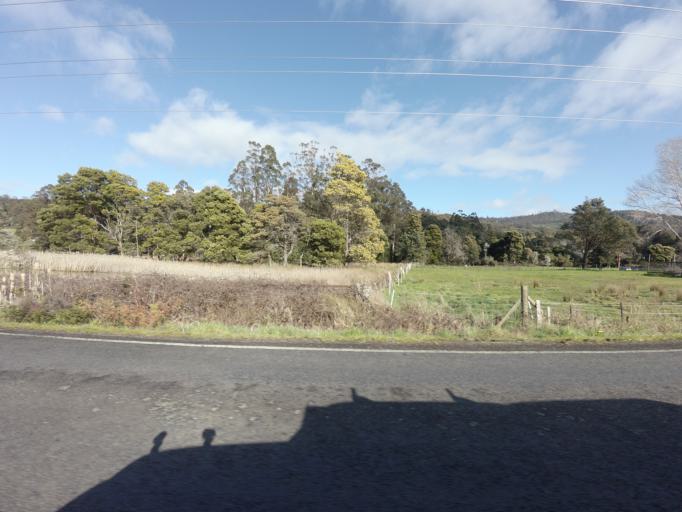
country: AU
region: Tasmania
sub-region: Huon Valley
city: Cygnet
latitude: -43.2901
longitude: 147.0108
